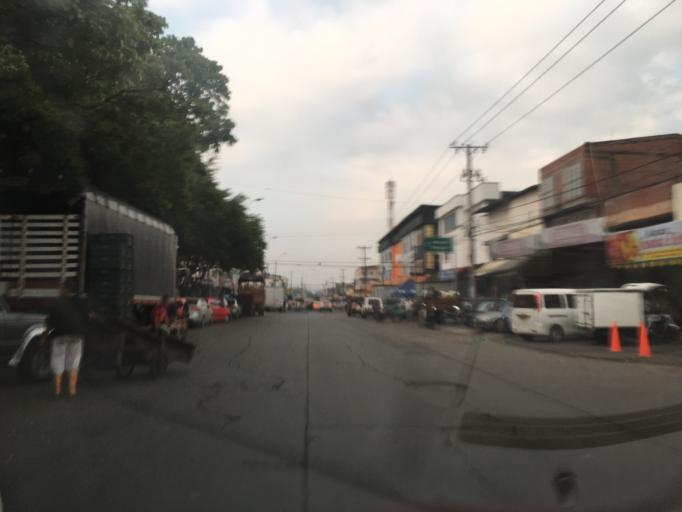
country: CO
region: Valle del Cauca
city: Cali
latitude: 3.4304
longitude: -76.5208
